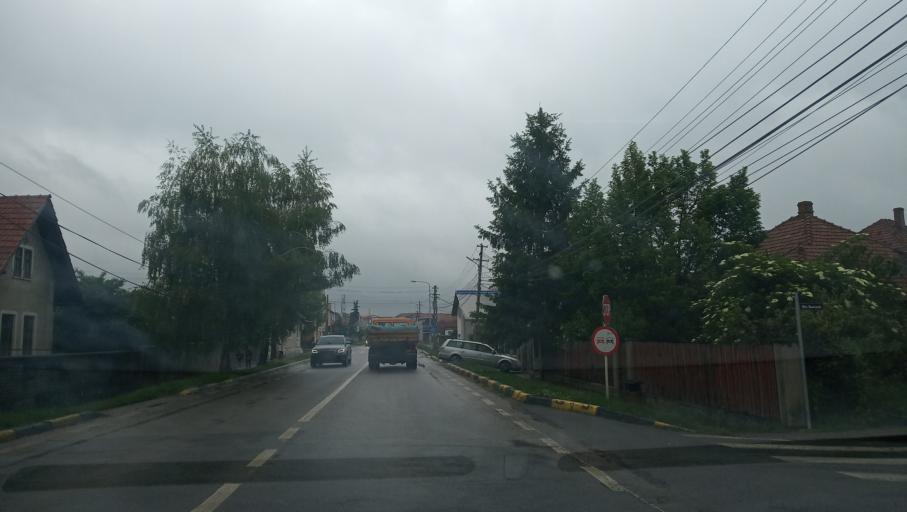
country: RO
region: Alba
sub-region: Municipiul Sebes
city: Sebes
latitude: 45.9521
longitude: 23.5814
